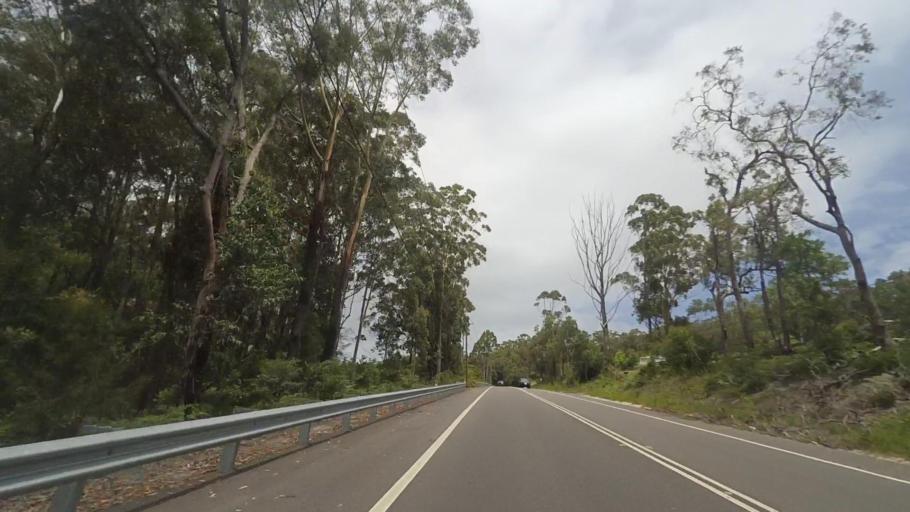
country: AU
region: New South Wales
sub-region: Wyong Shire
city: Chittaway Bay
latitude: -33.3331
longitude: 151.4118
